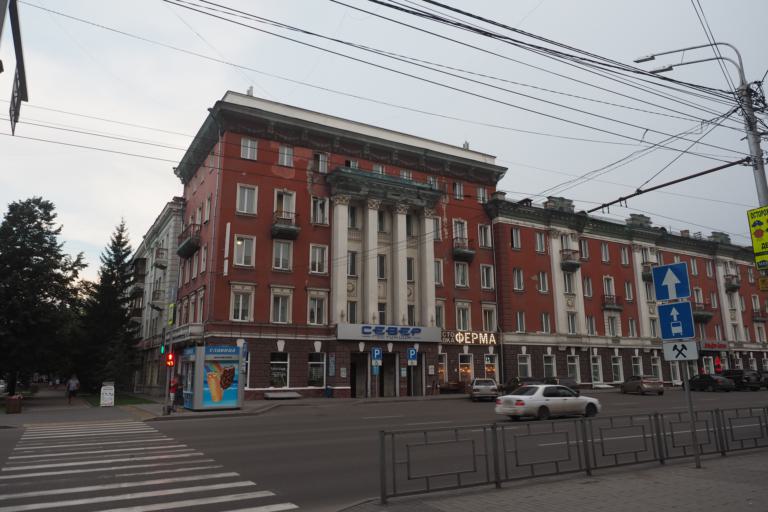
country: RU
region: Krasnoyarskiy
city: Krasnoyarsk
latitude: 56.0128
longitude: 92.8561
